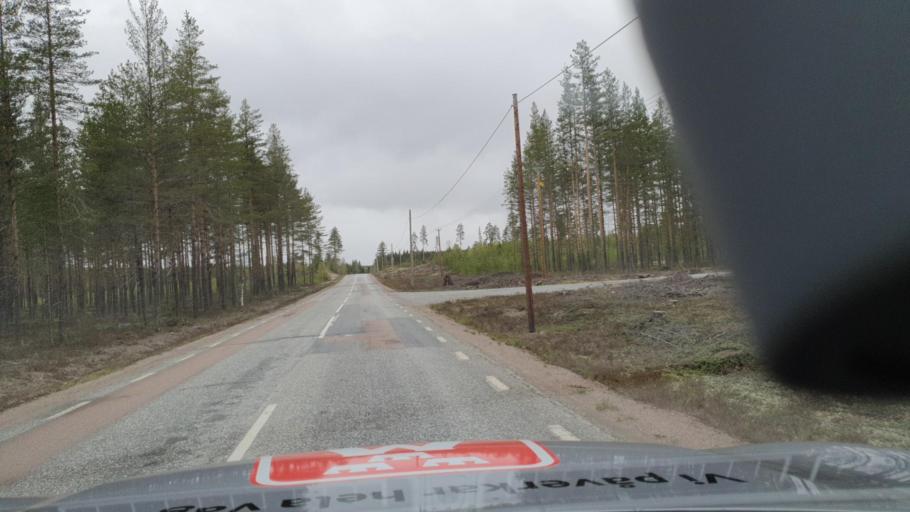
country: SE
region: Vaesternorrland
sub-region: Solleftea Kommun
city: Solleftea
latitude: 63.6042
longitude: 17.5359
